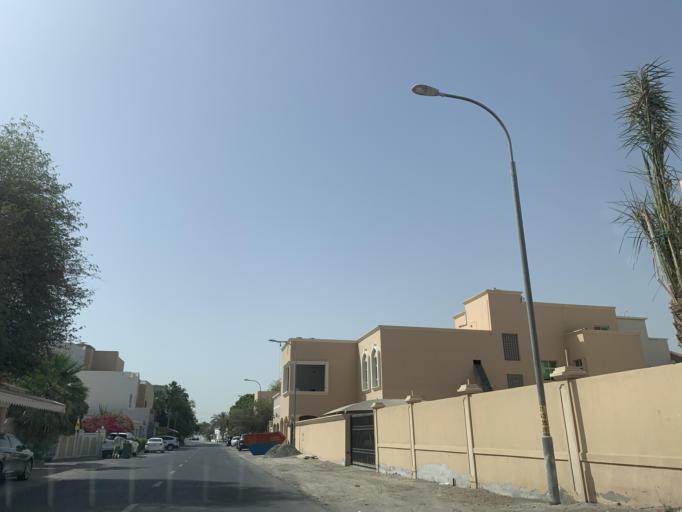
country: BH
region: Northern
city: Ar Rifa'
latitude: 26.1503
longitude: 50.5782
